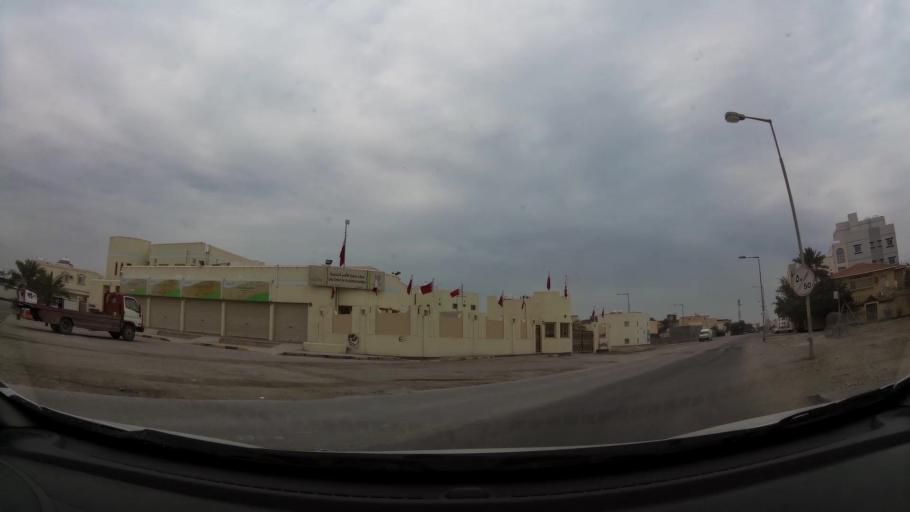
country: BH
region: Northern
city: Sitrah
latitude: 26.1608
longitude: 50.6184
